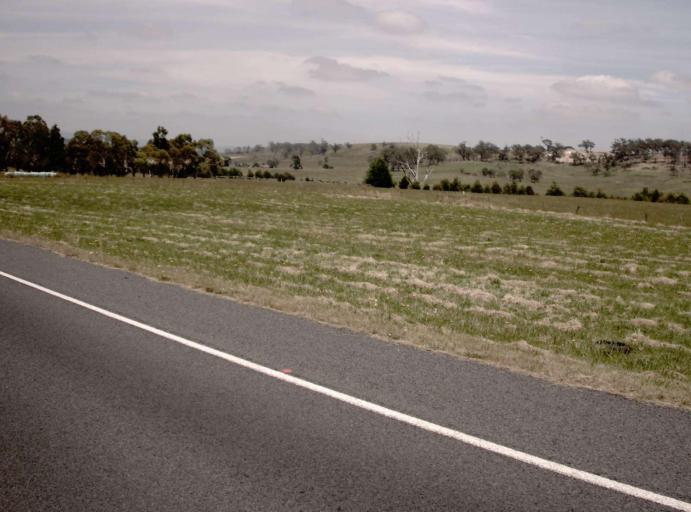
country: AU
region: Victoria
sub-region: Latrobe
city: Traralgon
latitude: -38.2313
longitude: 146.5404
